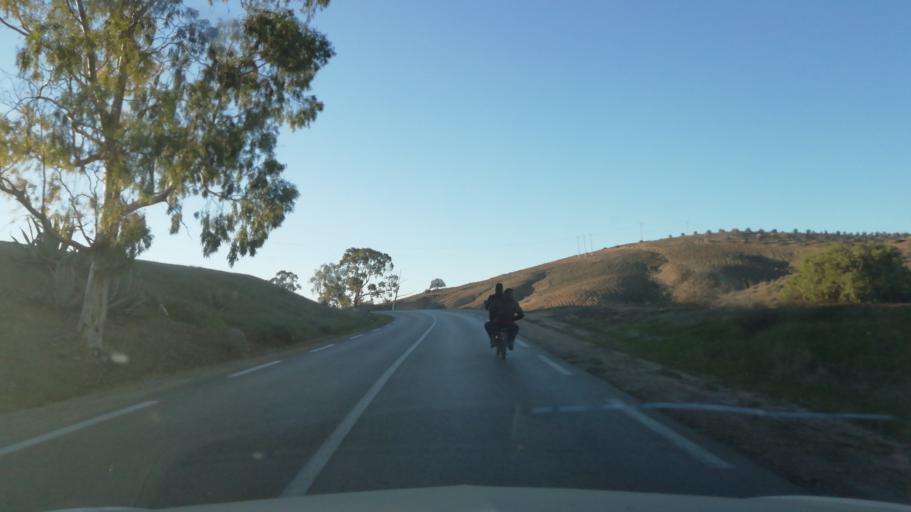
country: DZ
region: Tlemcen
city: Nedroma
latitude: 34.8276
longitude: -1.6588
